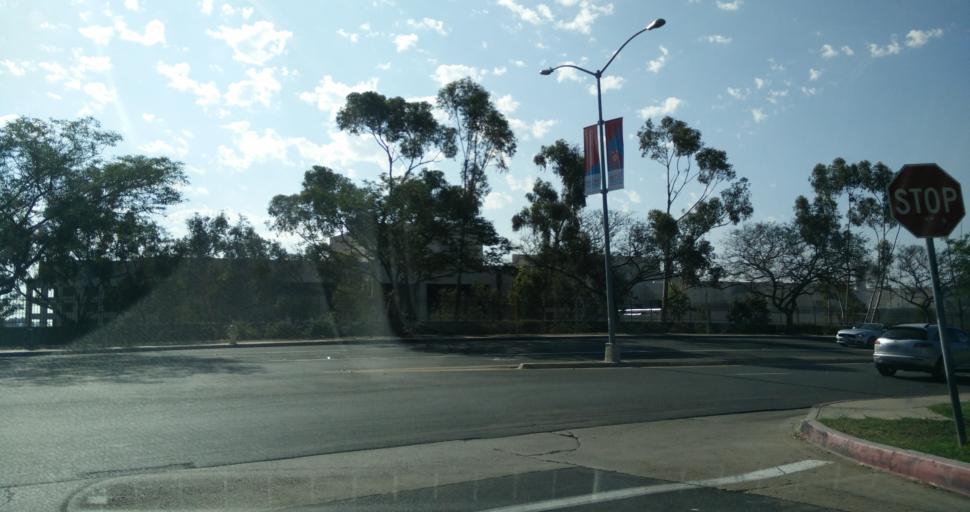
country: US
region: California
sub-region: San Diego County
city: San Diego
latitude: 32.7296
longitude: -117.1465
